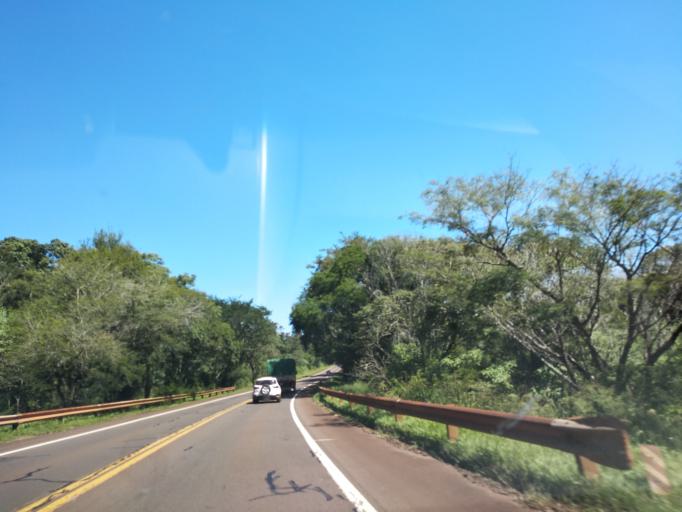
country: AR
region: Misiones
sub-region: Departamento de Iguazu
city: Puerto Iguazu
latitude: -25.7175
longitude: -54.5206
